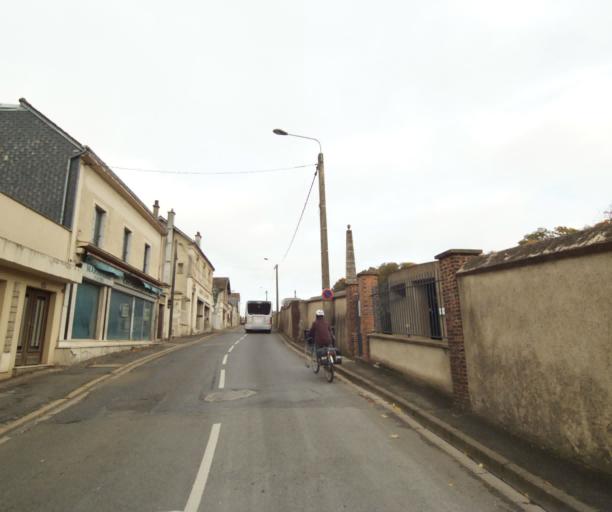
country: FR
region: Centre
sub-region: Departement d'Eure-et-Loir
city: Dreux
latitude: 48.7395
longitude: 1.3628
